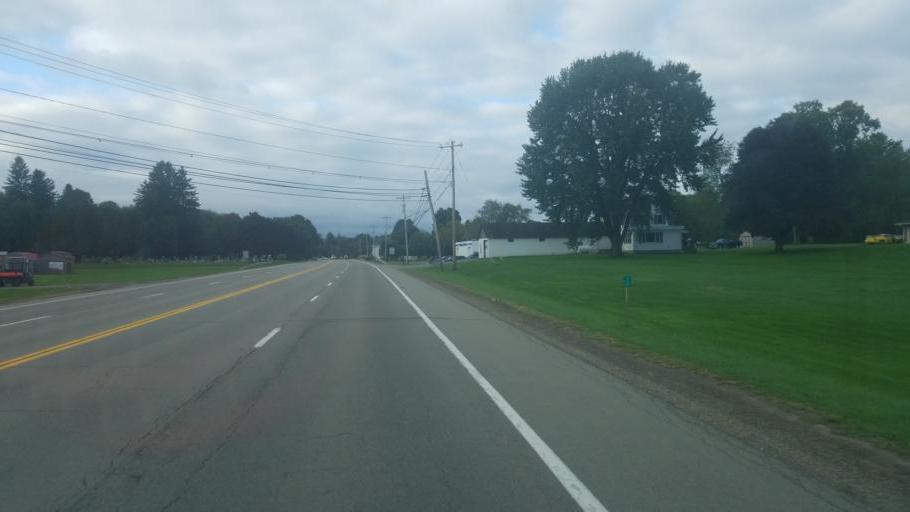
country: US
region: New York
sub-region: Cattaraugus County
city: Olean
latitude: 42.1274
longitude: -78.4115
